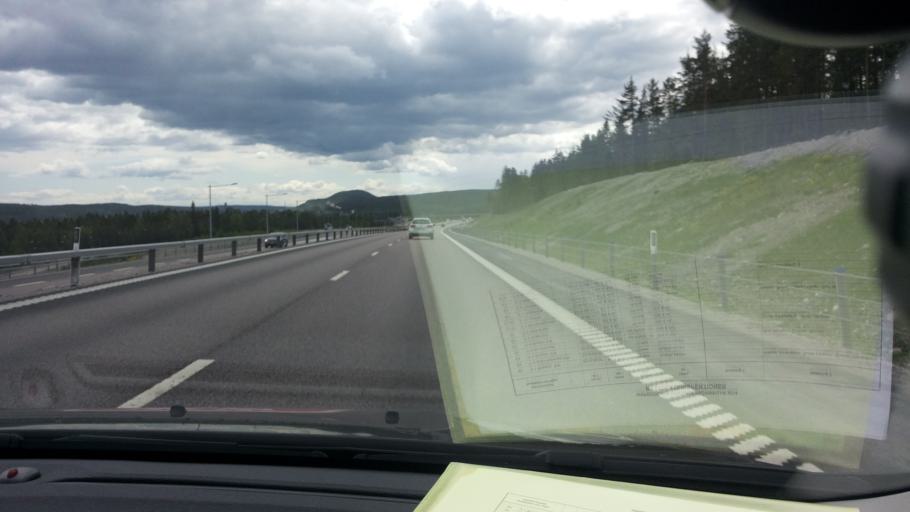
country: SE
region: Vaesternorrland
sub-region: Sundsvalls Kommun
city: Stockvik
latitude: 62.3619
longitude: 17.3668
